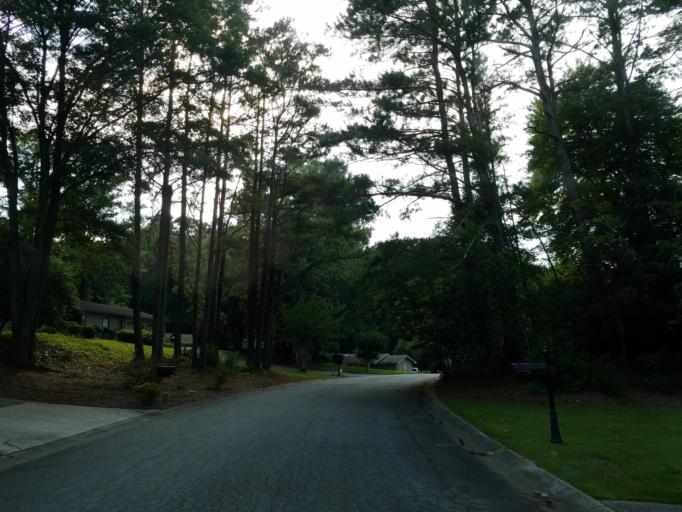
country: US
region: Georgia
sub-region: Fulton County
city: Sandy Springs
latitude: 33.9590
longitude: -84.4494
